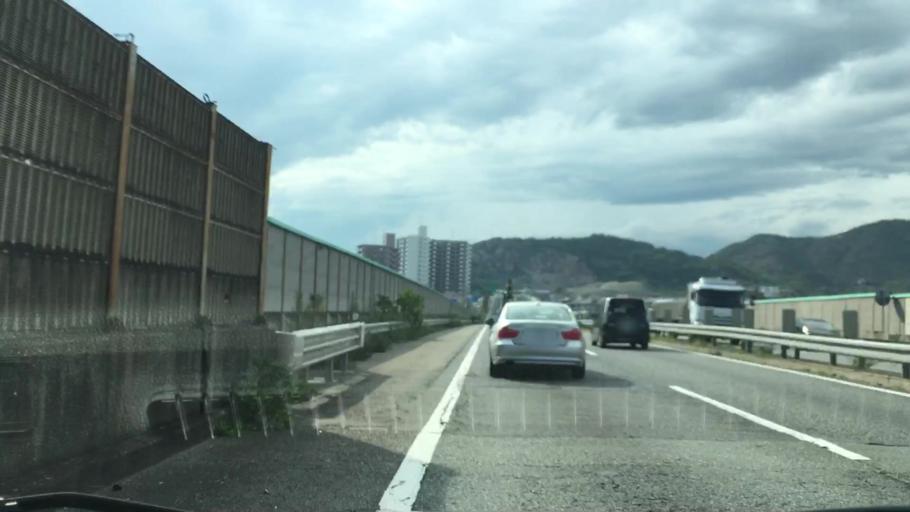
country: JP
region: Hyogo
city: Kakogawacho-honmachi
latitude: 34.7898
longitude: 134.8114
